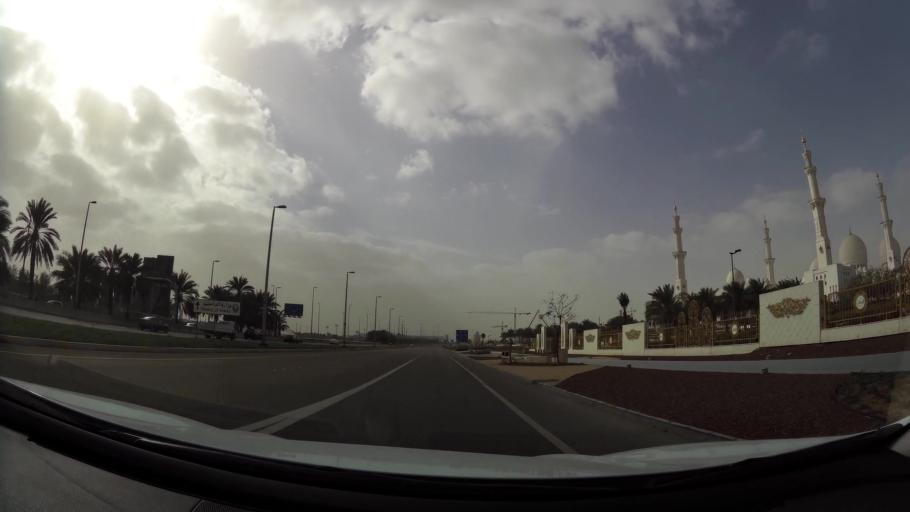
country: AE
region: Abu Dhabi
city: Abu Dhabi
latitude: 24.4145
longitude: 54.4778
